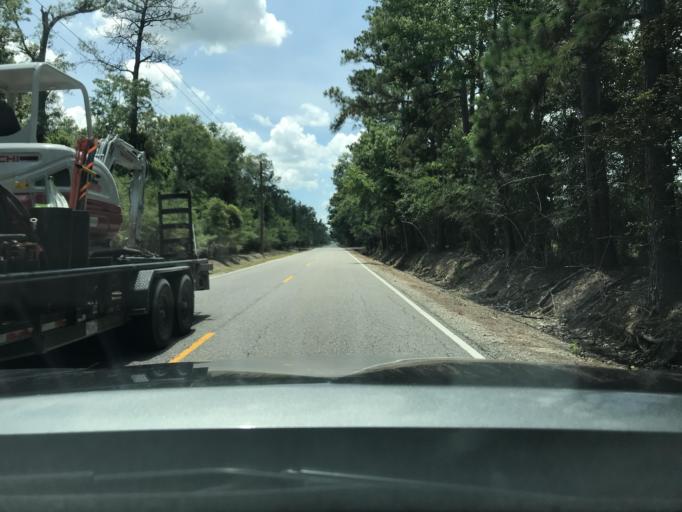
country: US
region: Louisiana
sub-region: Calcasieu Parish
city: Moss Bluff
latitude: 30.3301
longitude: -93.1581
